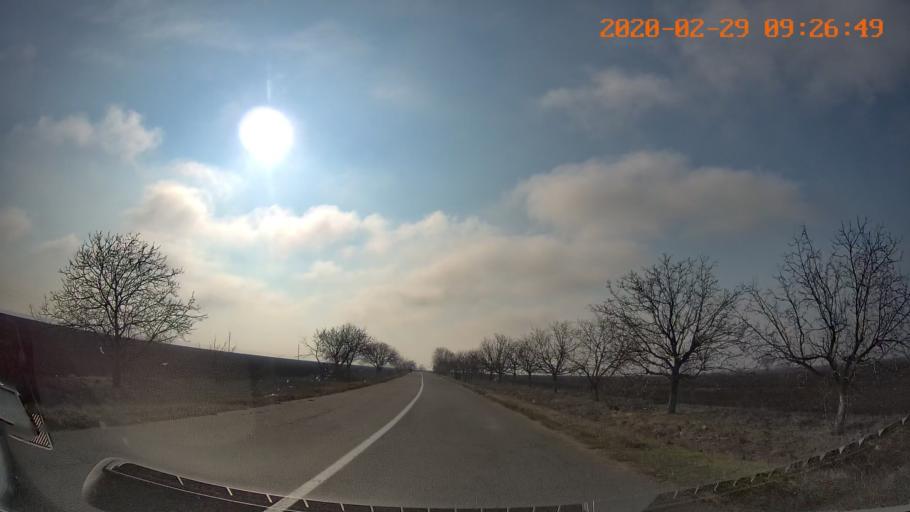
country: MD
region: Telenesti
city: Pervomaisc
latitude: 46.7018
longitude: 29.9449
